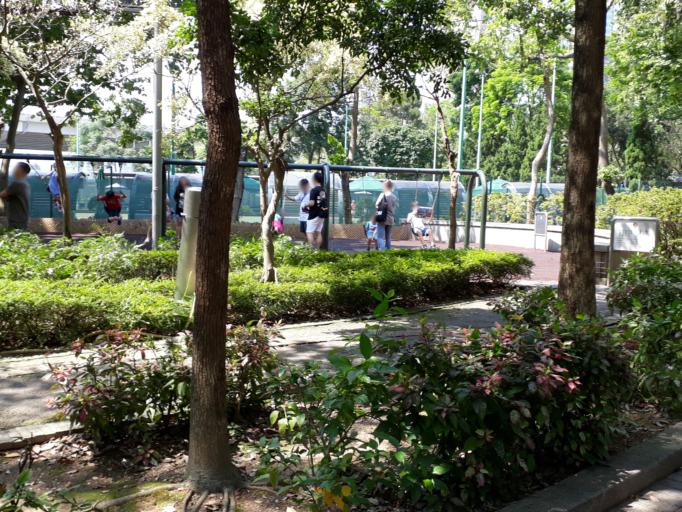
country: HK
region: Wanchai
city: Wan Chai
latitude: 22.2835
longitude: 114.1893
